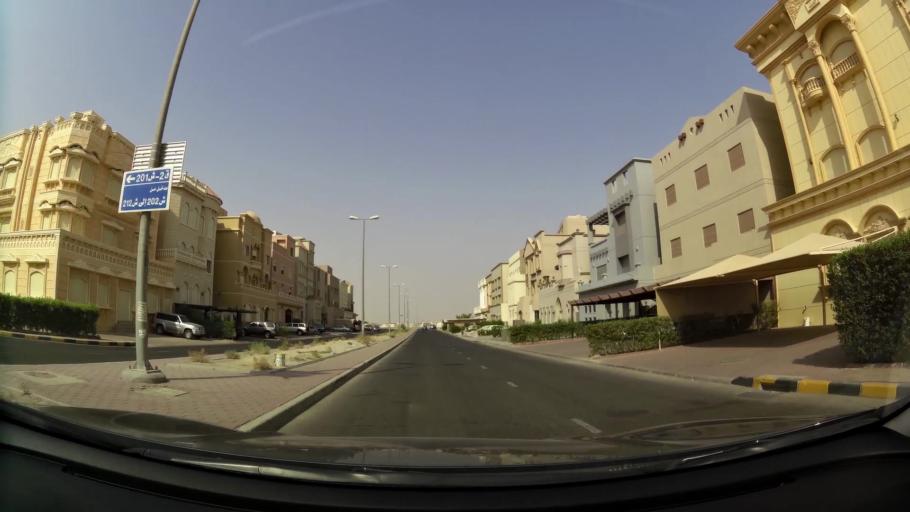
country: KW
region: Muhafazat al Jahra'
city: Al Jahra'
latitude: 29.3368
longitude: 47.7624
